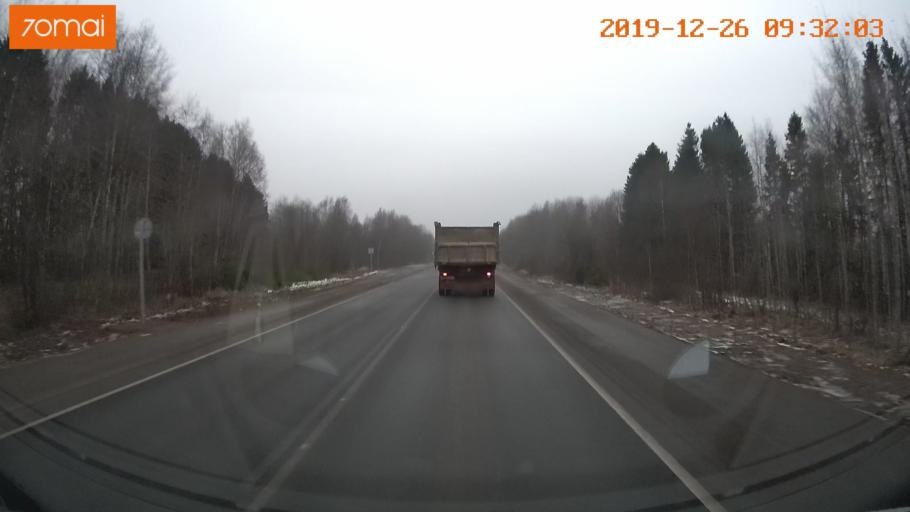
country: RU
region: Vologda
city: Gryazovets
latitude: 59.0743
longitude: 40.1211
